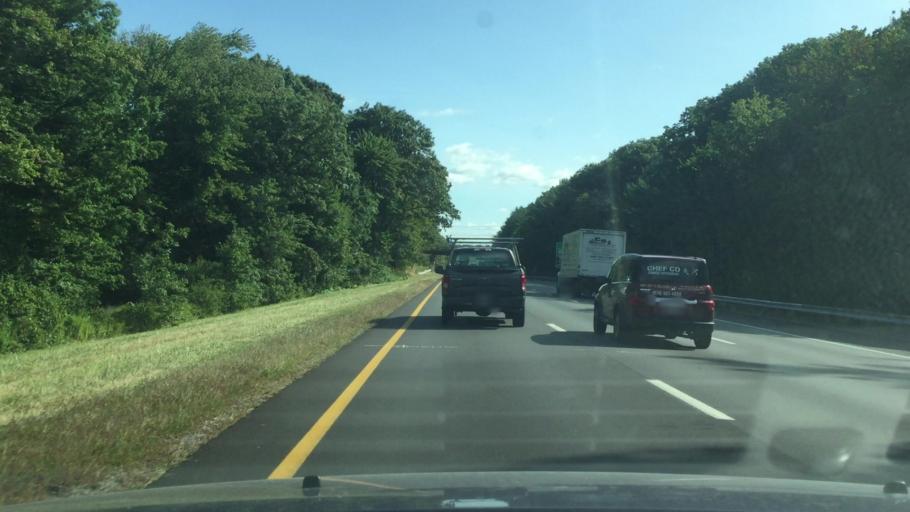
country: US
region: Massachusetts
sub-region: Essex County
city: Lawrence
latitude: 42.6700
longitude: -71.1835
